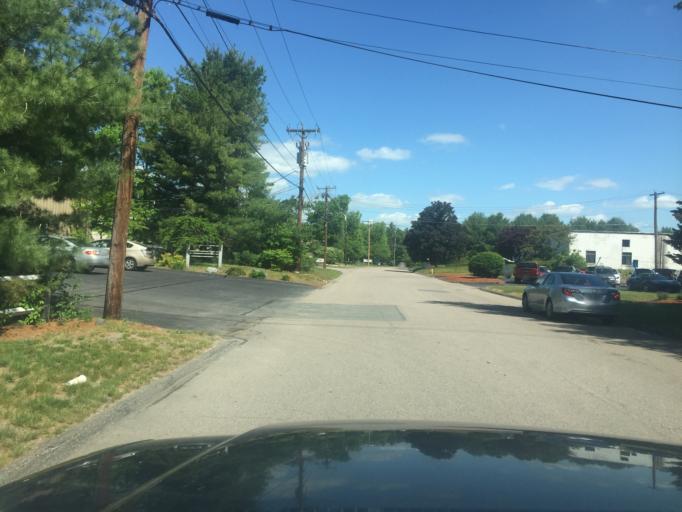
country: US
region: Massachusetts
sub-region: Norfolk County
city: Medway
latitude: 42.1571
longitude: -71.3921
